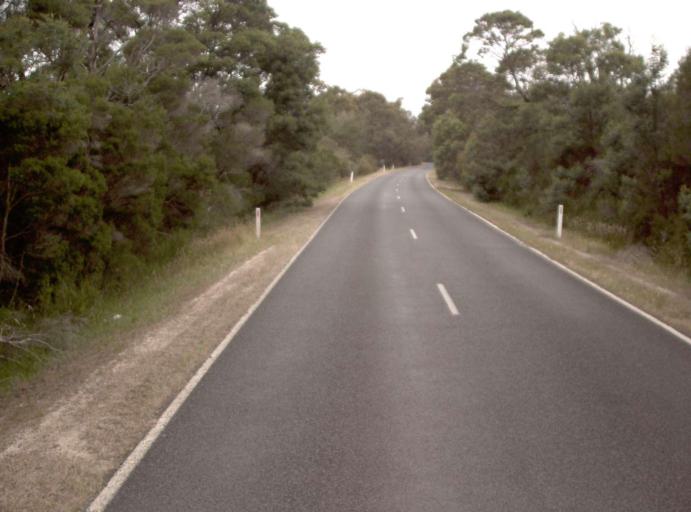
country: AU
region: Victoria
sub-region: Latrobe
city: Traralgon
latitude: -38.5073
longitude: 146.8456
